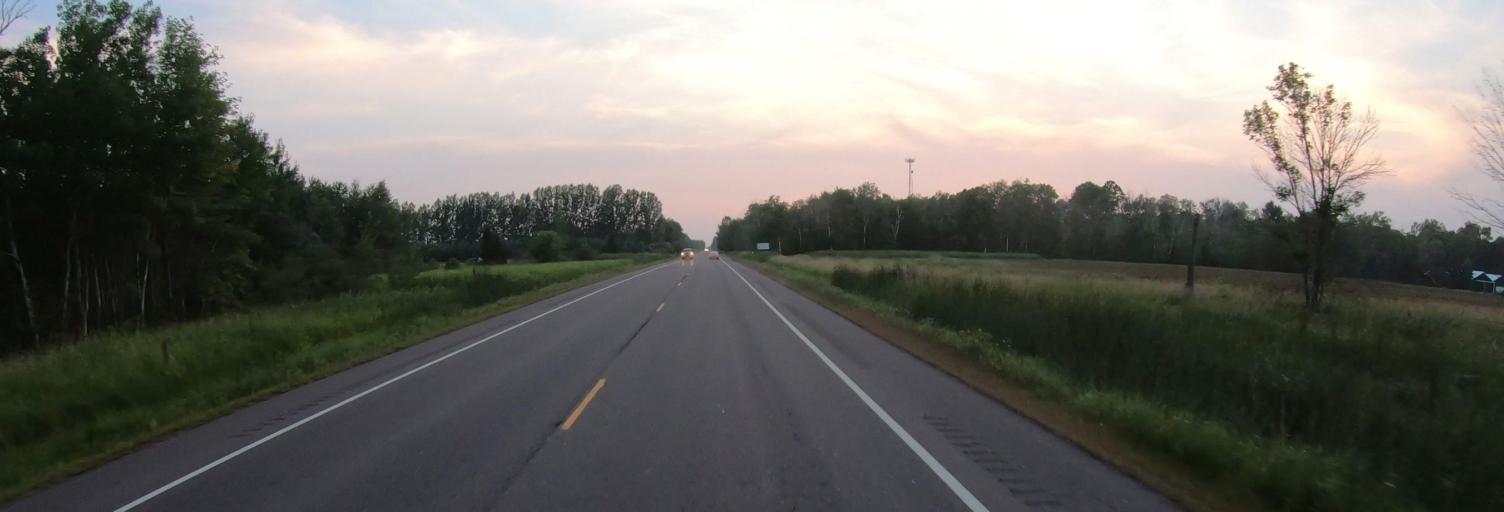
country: US
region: Minnesota
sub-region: Pine County
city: Rock Creek
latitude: 45.7734
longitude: -92.8643
